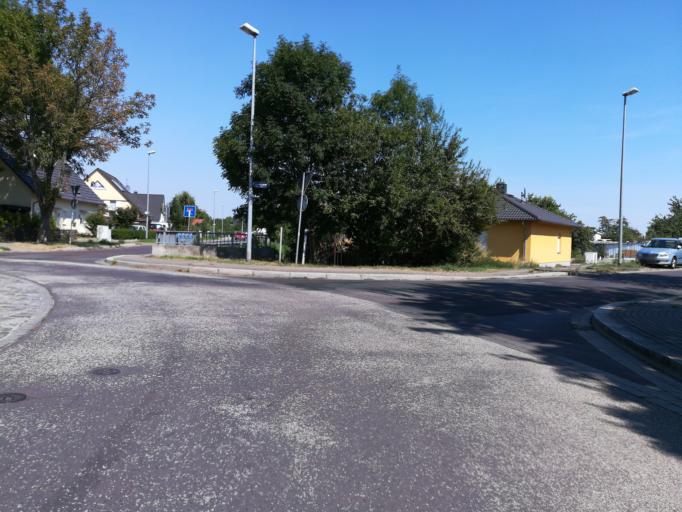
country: DE
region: Saxony-Anhalt
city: Neue Neustadt
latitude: 52.1477
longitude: 11.6135
